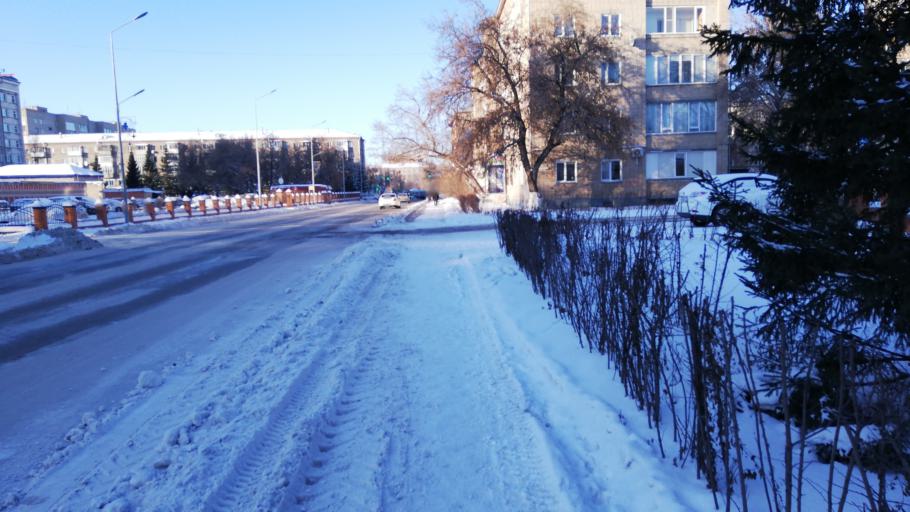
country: KZ
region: Soltustik Qazaqstan
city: Petropavlovsk
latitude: 54.8637
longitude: 69.1423
